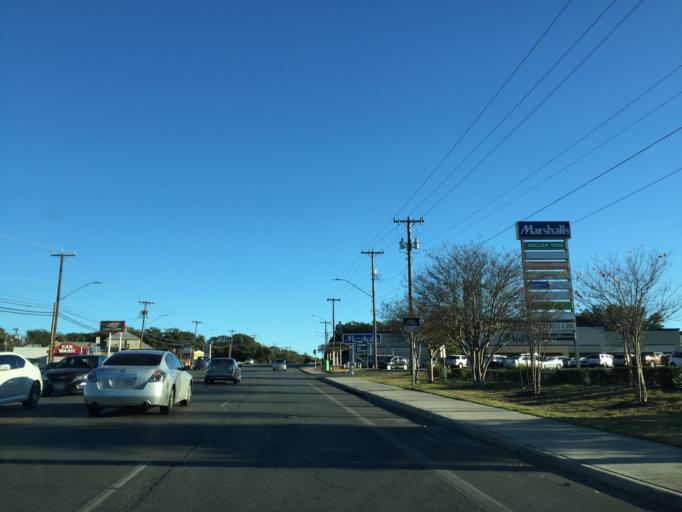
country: US
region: Texas
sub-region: Bexar County
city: Castle Hills
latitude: 29.5461
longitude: -98.5087
